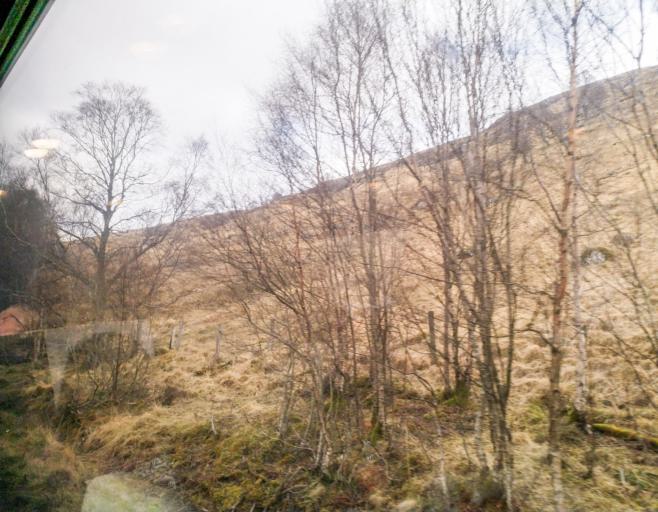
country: GB
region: Scotland
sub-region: Highland
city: Spean Bridge
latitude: 56.7914
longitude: -4.7269
